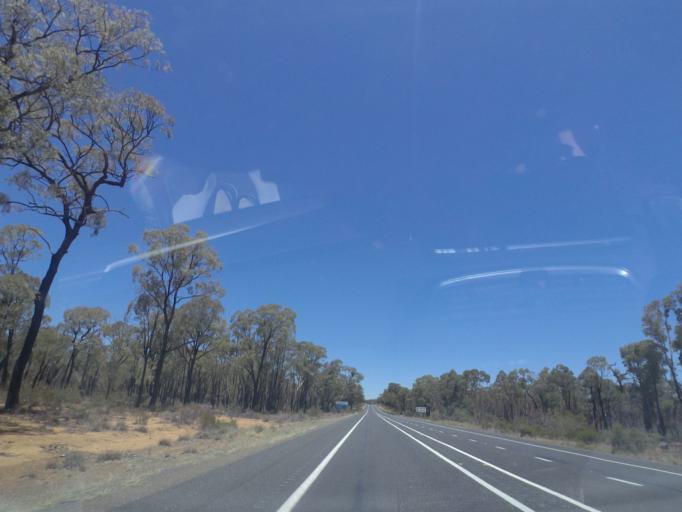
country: AU
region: New South Wales
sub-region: Warrumbungle Shire
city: Coonabarabran
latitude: -30.8797
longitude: 149.4468
